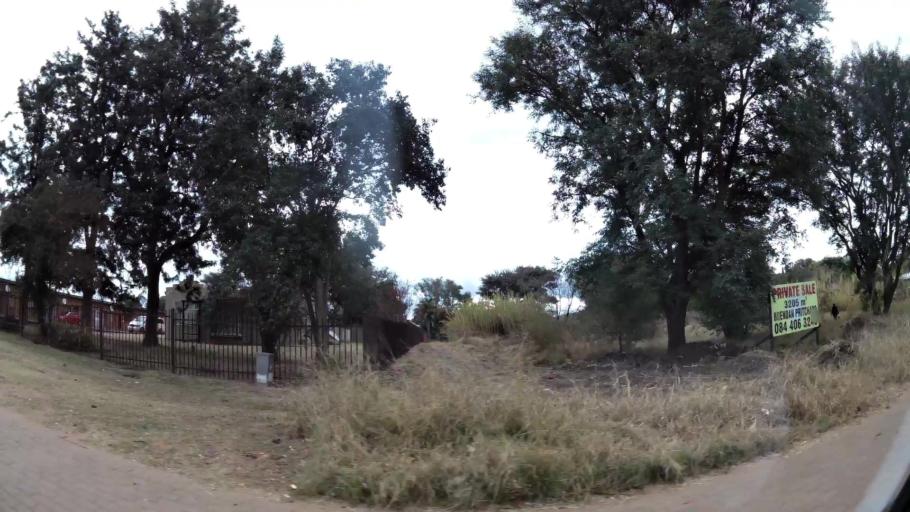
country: ZA
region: Limpopo
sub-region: Waterberg District Municipality
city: Modimolle
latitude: -24.7027
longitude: 28.4127
